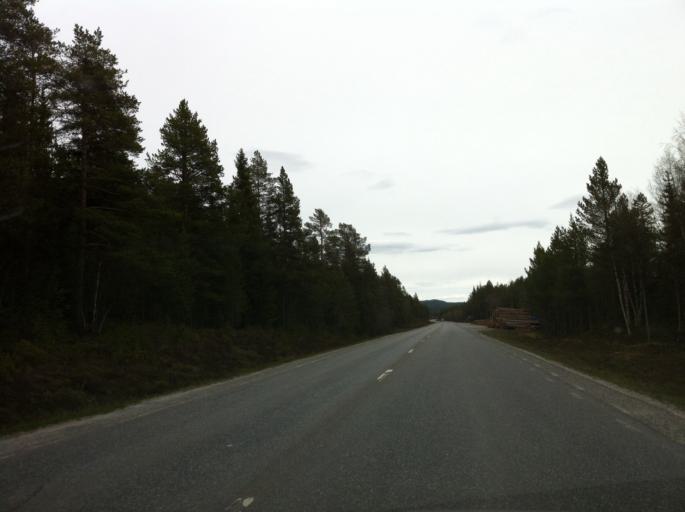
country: NO
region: Hedmark
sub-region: Engerdal
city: Engerdal
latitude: 62.5339
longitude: 12.5598
